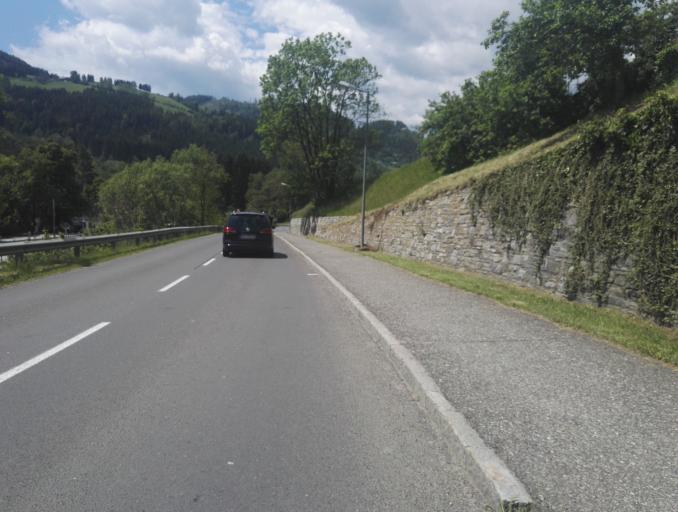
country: AT
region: Styria
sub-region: Politischer Bezirk Graz-Umgebung
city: Ubelbach
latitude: 47.2195
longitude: 15.2576
